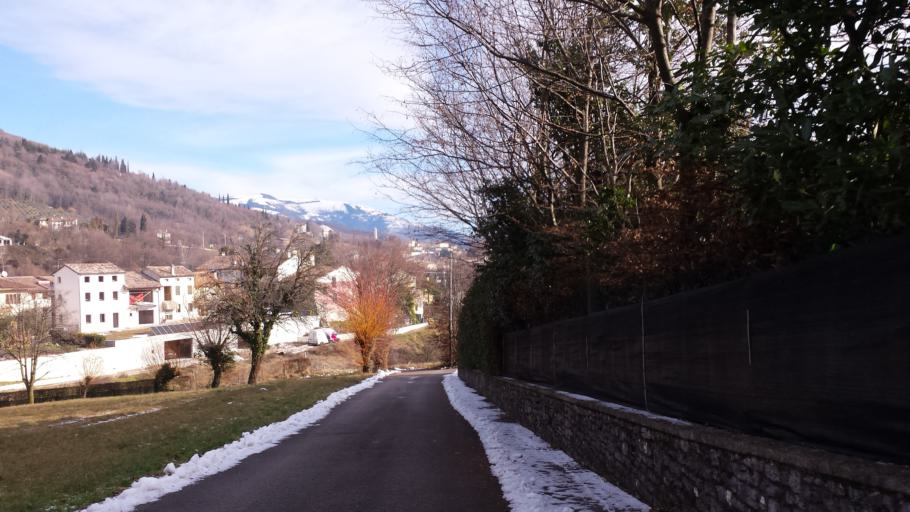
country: IT
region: Veneto
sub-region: Provincia di Treviso
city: Possagno
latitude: 45.8506
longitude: 11.8638
